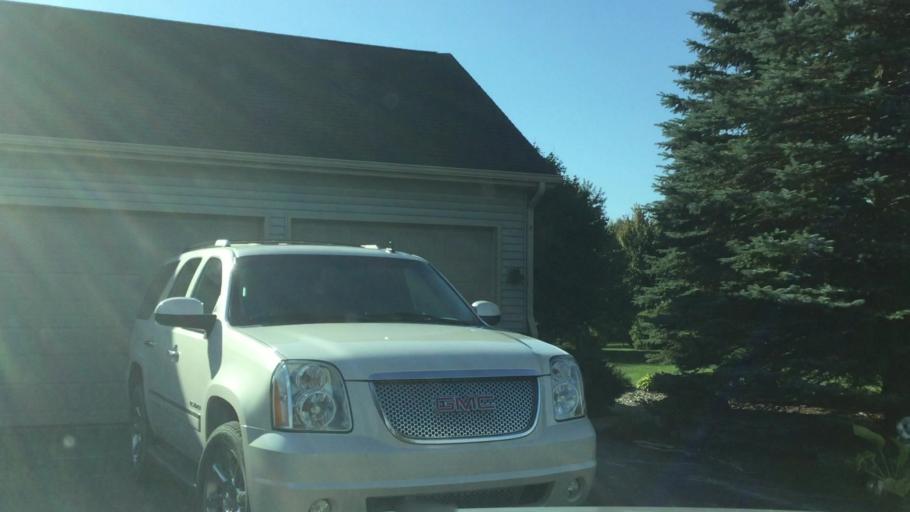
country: US
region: Michigan
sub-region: Livingston County
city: Howell
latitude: 42.6057
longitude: -83.8656
